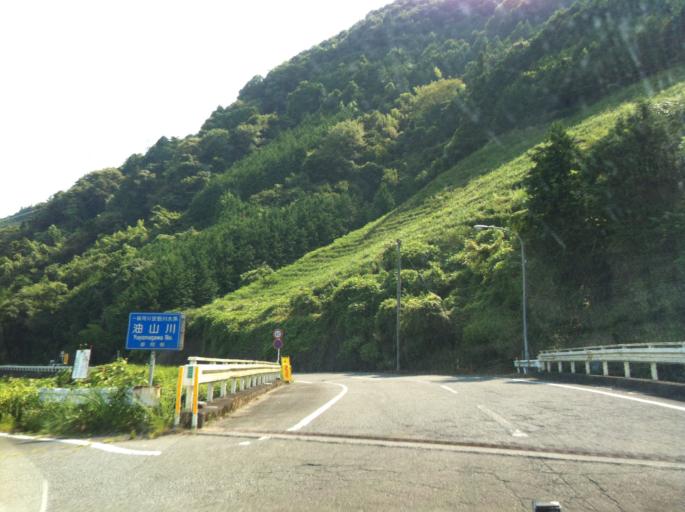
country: JP
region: Shizuoka
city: Shizuoka-shi
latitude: 35.0647
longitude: 138.3598
